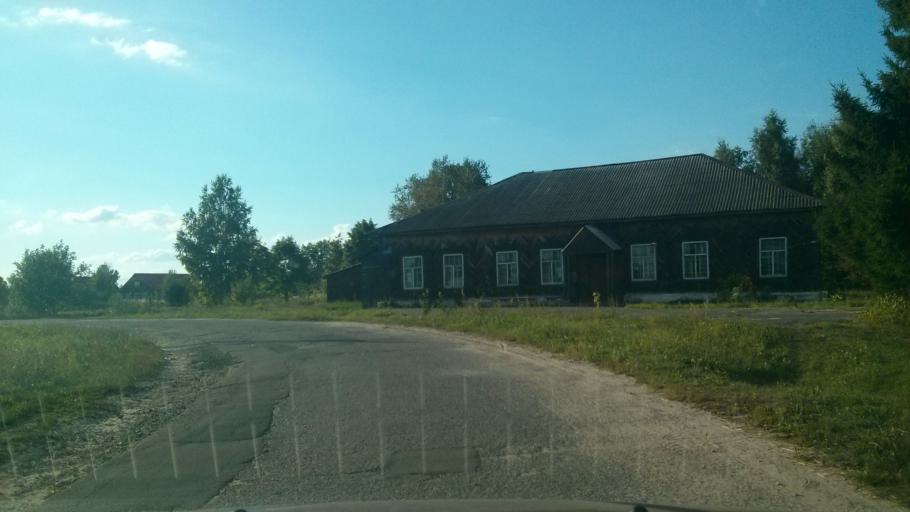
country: RU
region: Vladimir
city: Melenki
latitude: 55.2950
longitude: 41.8062
